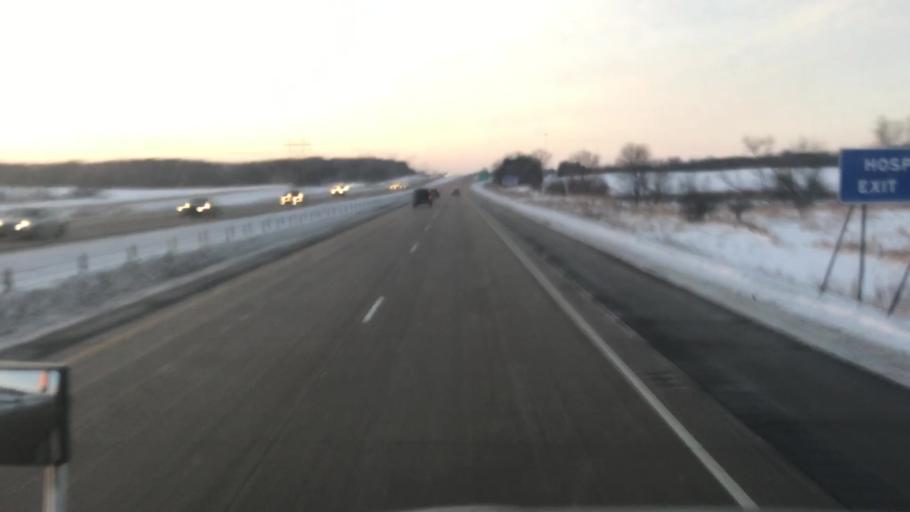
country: US
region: Minnesota
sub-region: Scott County
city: Elko New Market
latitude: 44.4805
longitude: -93.2921
